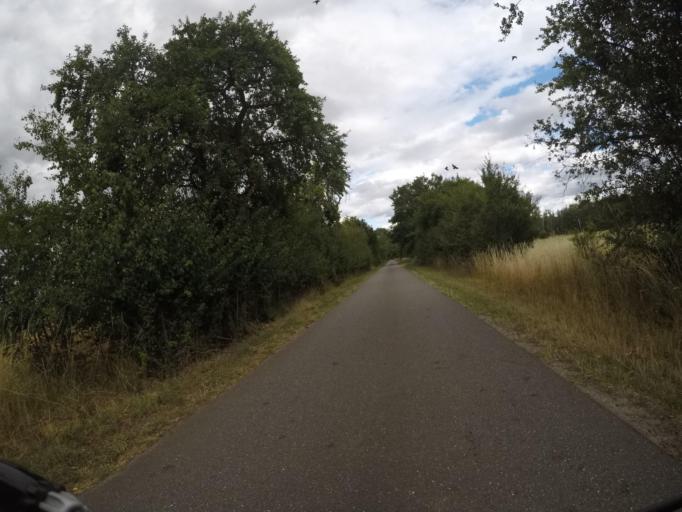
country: DE
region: Lower Saxony
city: Neu Darchau
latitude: 53.2393
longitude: 10.9032
